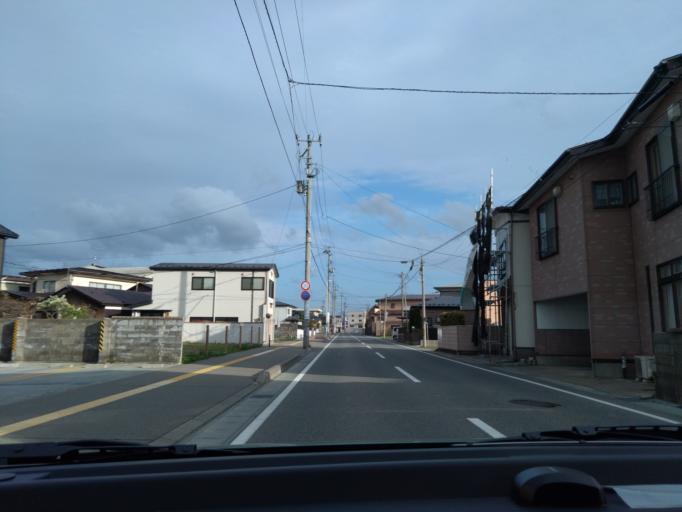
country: JP
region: Akita
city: Akita Shi
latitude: 39.7576
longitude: 140.0735
